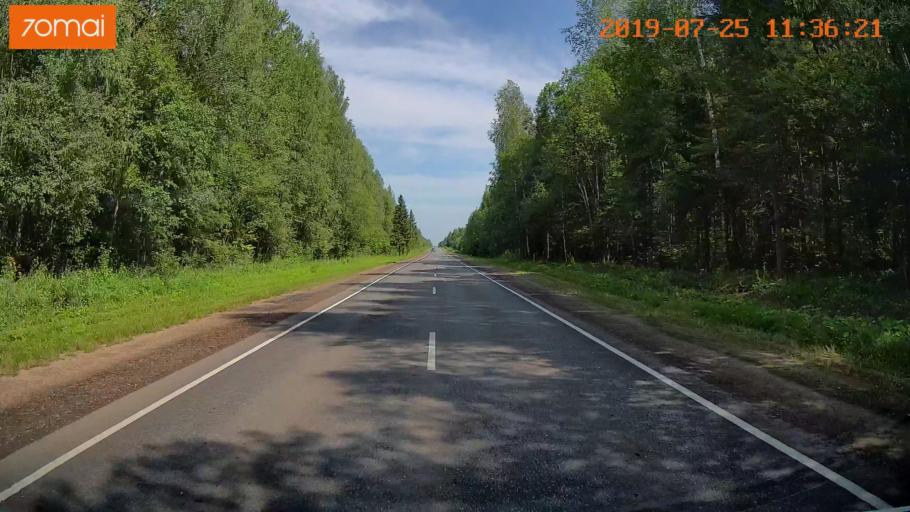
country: RU
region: Ivanovo
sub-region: Privolzhskiy Rayon
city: Ples
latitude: 57.4219
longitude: 41.4469
